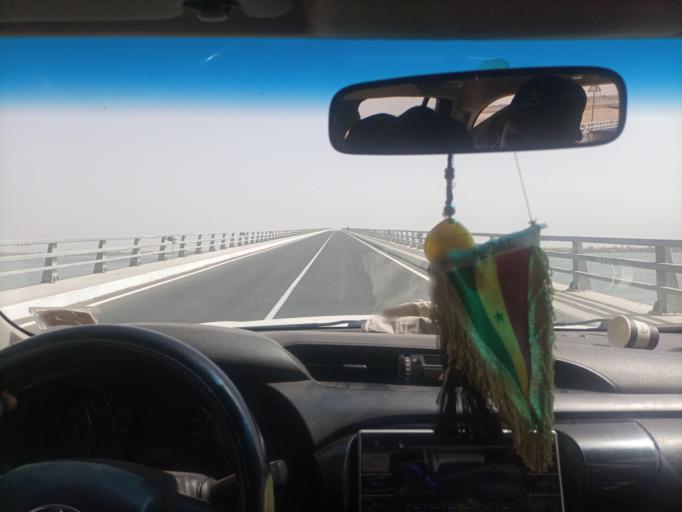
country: SN
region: Fatick
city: Foundiougne
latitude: 14.1412
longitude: -16.4712
